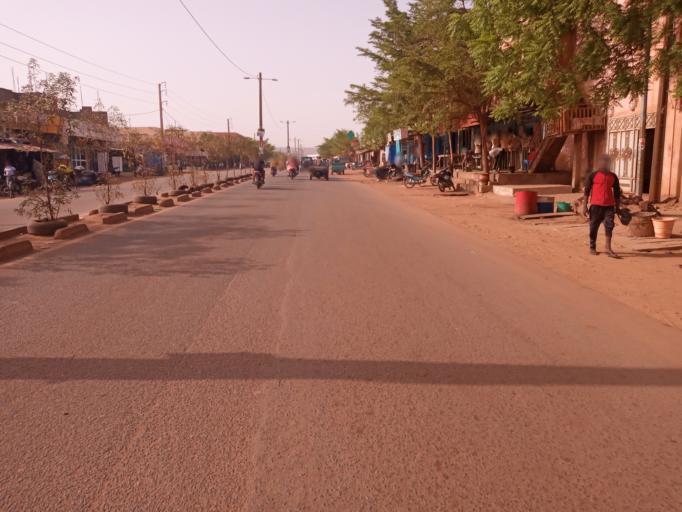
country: ML
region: Bamako
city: Bamako
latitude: 12.6748
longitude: -7.9434
